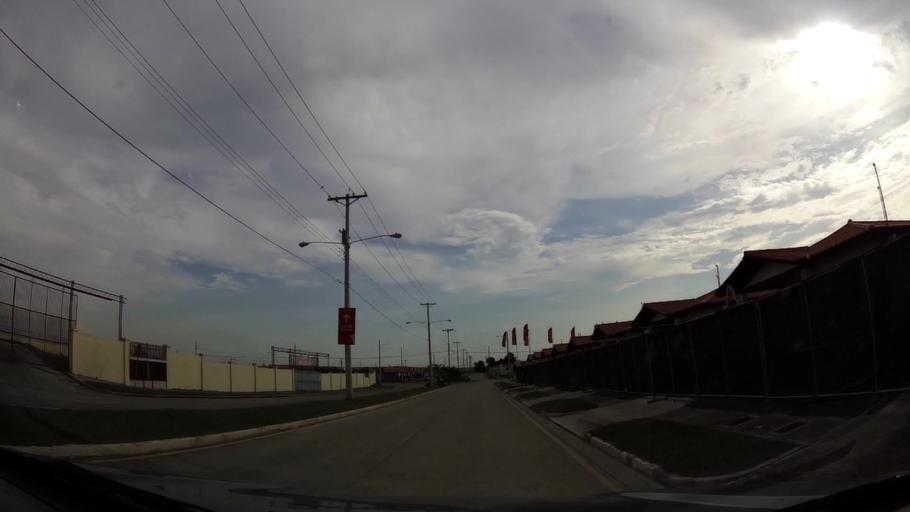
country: PA
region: Panama
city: Tocumen
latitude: 9.0715
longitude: -79.3648
